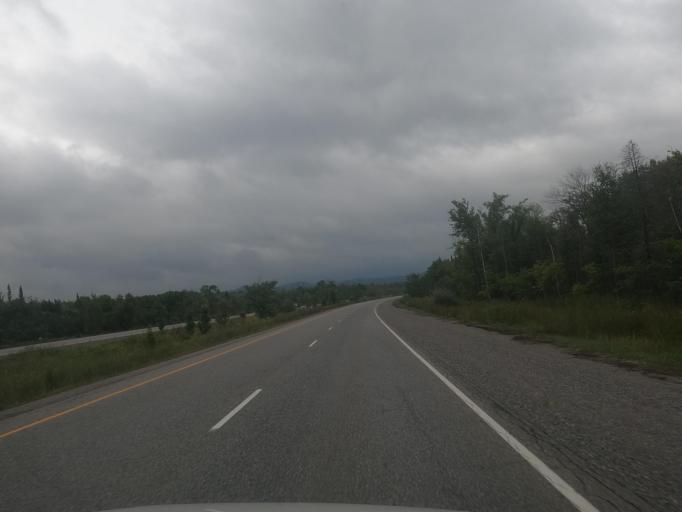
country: CA
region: Ontario
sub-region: Algoma
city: Sault Ste. Marie
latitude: 46.5170
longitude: -84.0610
